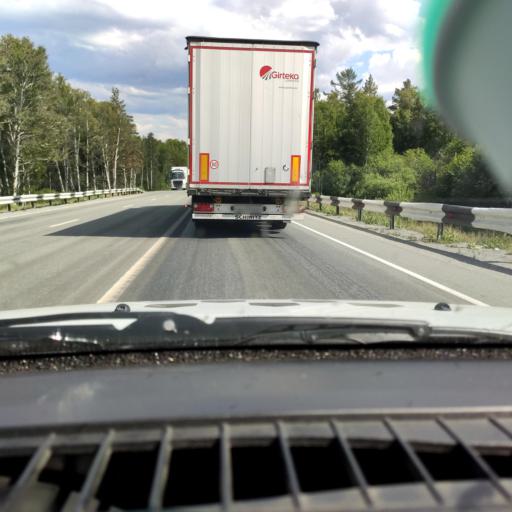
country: RU
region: Chelyabinsk
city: Syrostan
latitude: 55.0119
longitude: 59.7998
